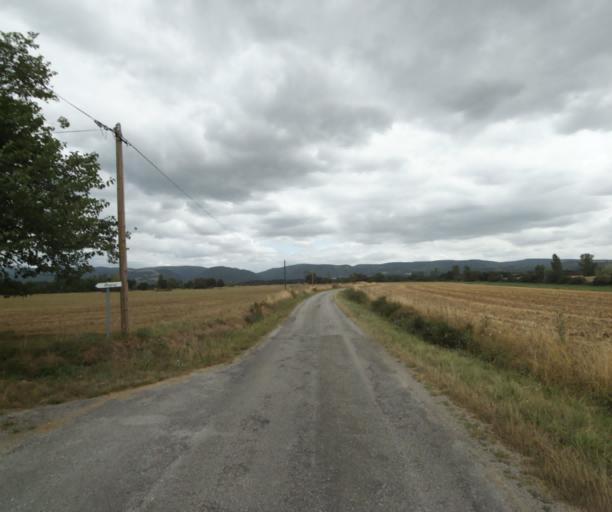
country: FR
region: Midi-Pyrenees
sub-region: Departement de la Haute-Garonne
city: Revel
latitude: 43.4829
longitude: 2.0295
